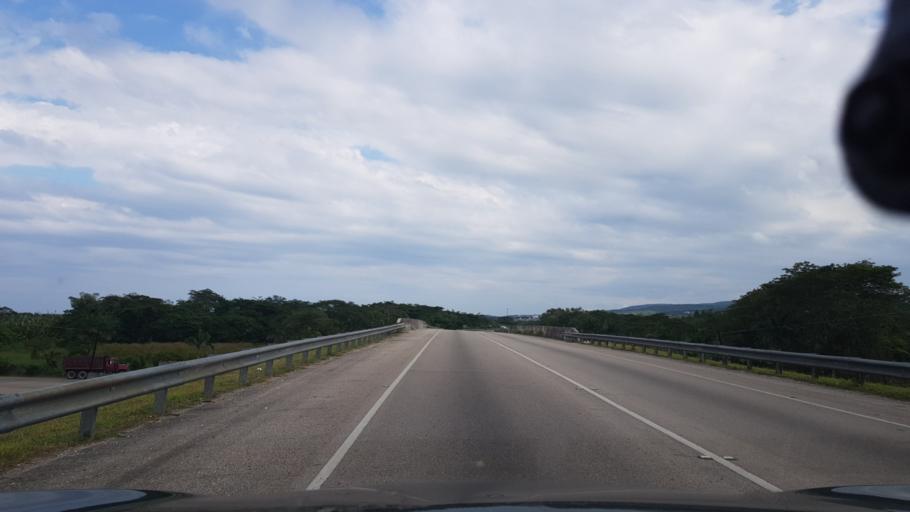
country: JM
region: Trelawny
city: Falmouth
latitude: 18.4765
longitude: -77.6598
